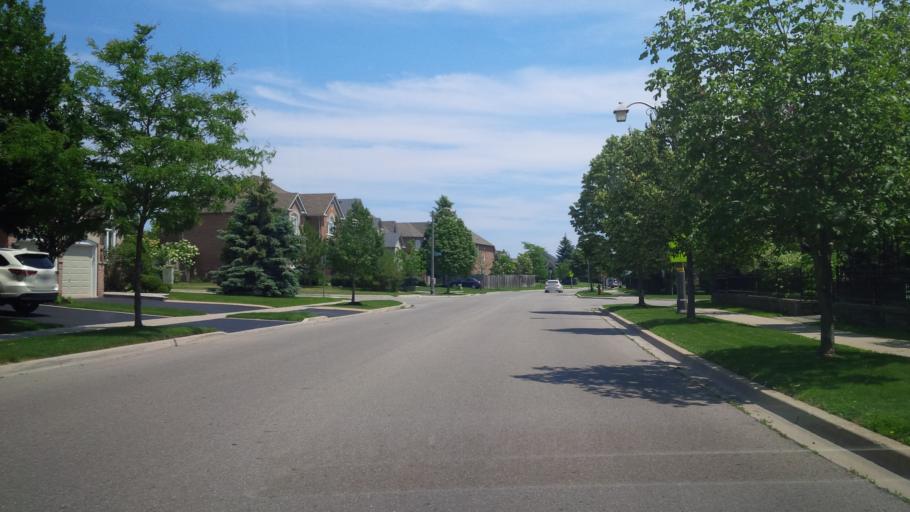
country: CA
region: Ontario
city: Burlington
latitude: 43.3987
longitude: -79.8061
